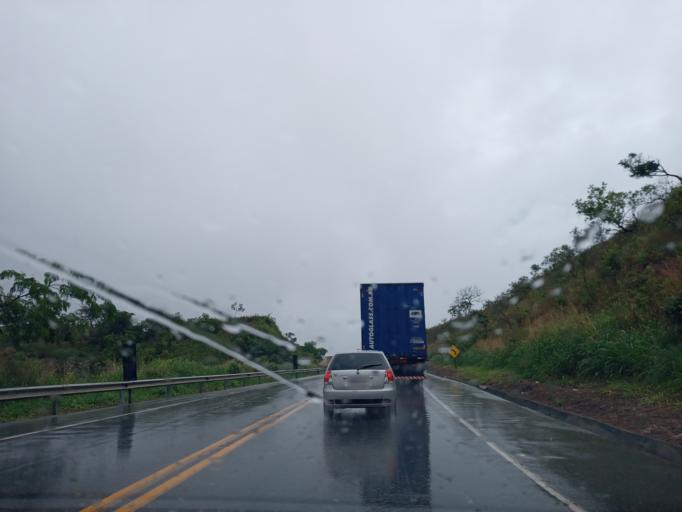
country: BR
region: Minas Gerais
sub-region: Luz
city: Luz
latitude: -19.7183
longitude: -45.8818
